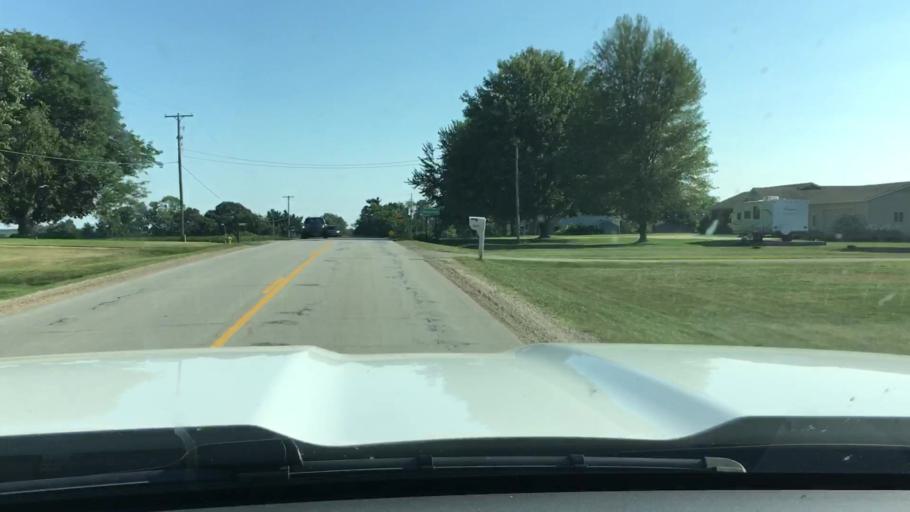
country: US
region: Michigan
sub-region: Ottawa County
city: Zeeland
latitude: 42.8527
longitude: -85.9600
